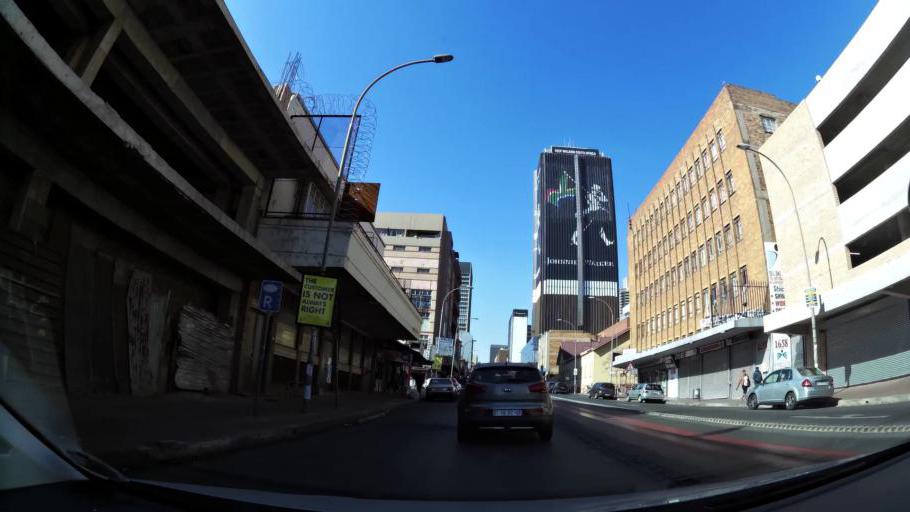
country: ZA
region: Gauteng
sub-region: City of Johannesburg Metropolitan Municipality
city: Johannesburg
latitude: -26.2055
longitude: 28.0339
